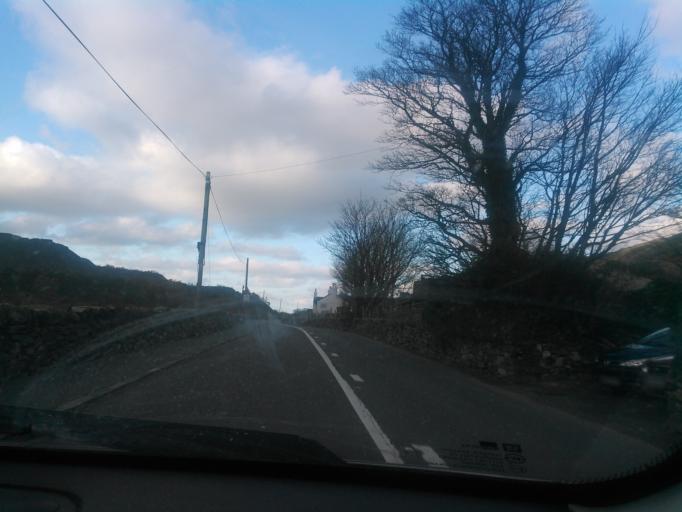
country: GB
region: Wales
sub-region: Gwynedd
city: Bethesda
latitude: 53.1536
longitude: -4.0418
